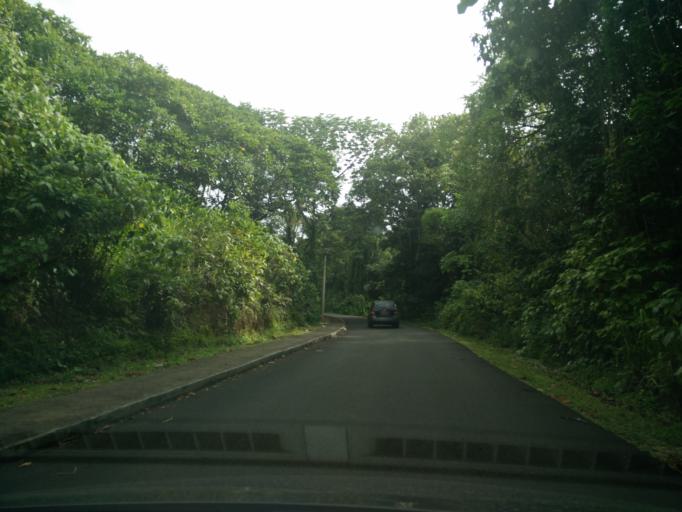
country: GP
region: Guadeloupe
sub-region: Guadeloupe
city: Petit-Bourg
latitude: 16.1922
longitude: -61.6580
